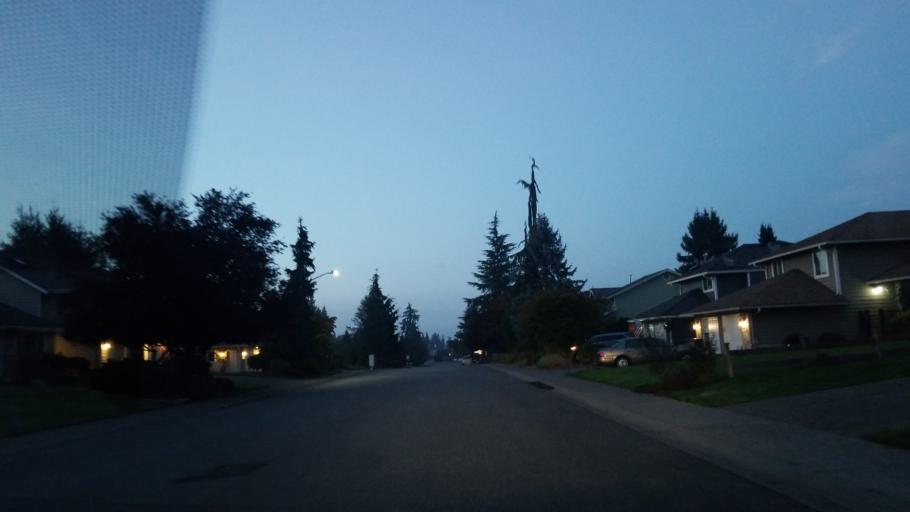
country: US
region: Washington
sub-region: Snohomish County
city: Silver Firs
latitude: 47.8853
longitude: -122.1715
